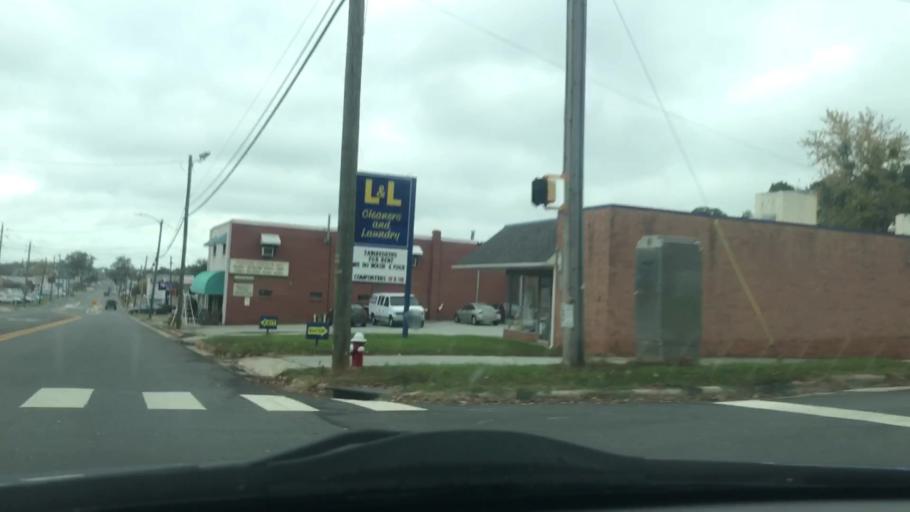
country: US
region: North Carolina
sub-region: Randolph County
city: Asheboro
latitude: 35.6908
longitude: -79.8159
